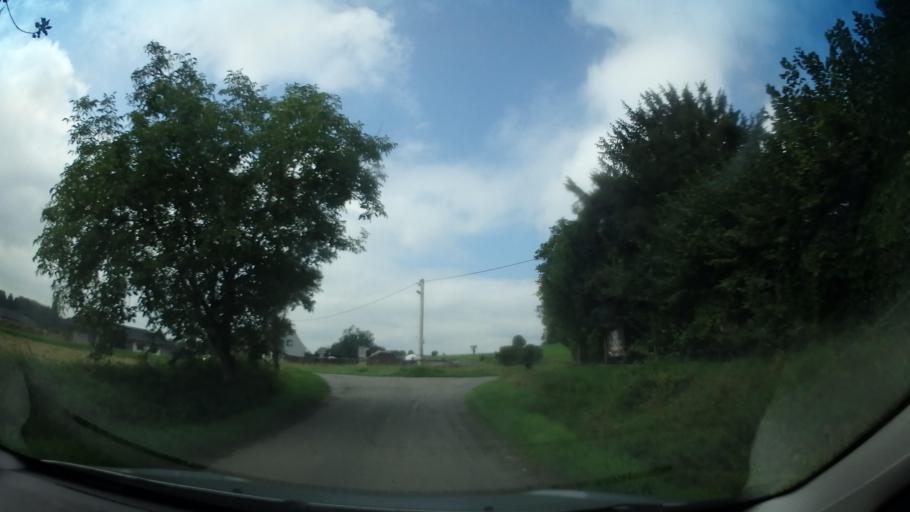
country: CZ
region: Central Bohemia
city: Sedlcany
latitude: 49.7048
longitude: 14.3565
